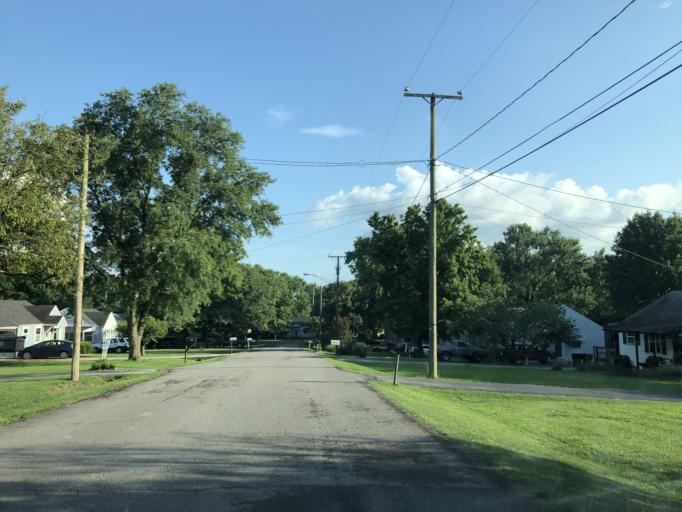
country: US
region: Tennessee
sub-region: Davidson County
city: Nashville
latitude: 36.1500
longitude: -86.7202
